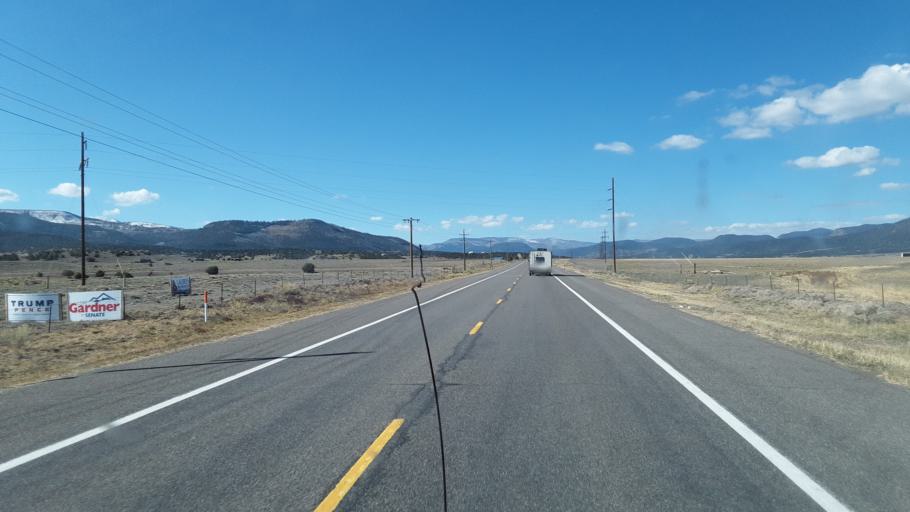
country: US
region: Colorado
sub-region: Rio Grande County
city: Del Norte
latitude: 37.6772
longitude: -106.4904
